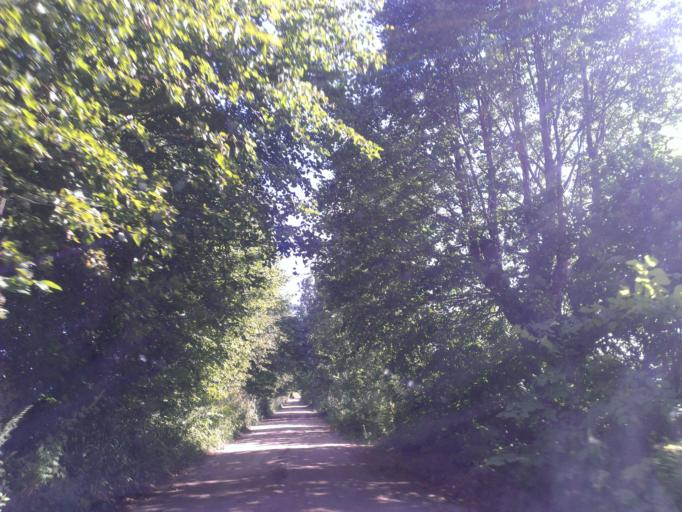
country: LV
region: Sigulda
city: Sigulda
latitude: 57.1724
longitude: 24.8878
